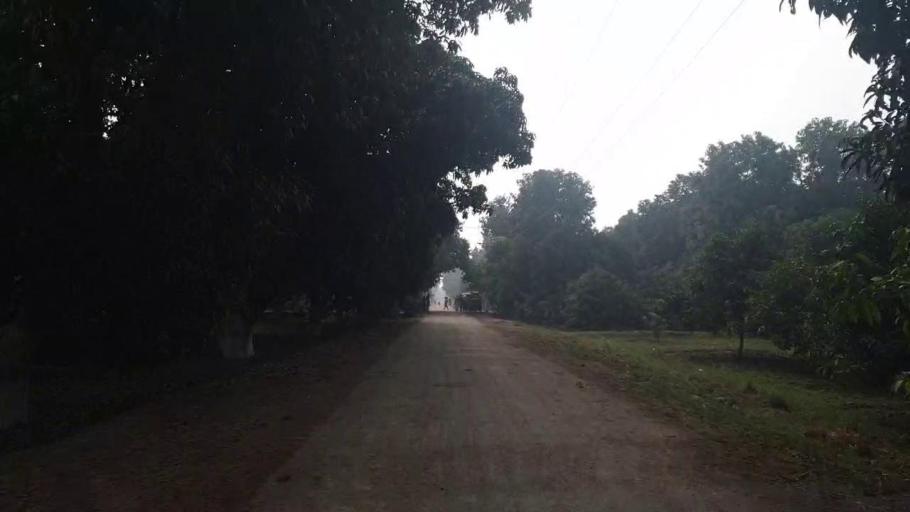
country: PK
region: Sindh
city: Tando Adam
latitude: 25.7862
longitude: 68.5962
